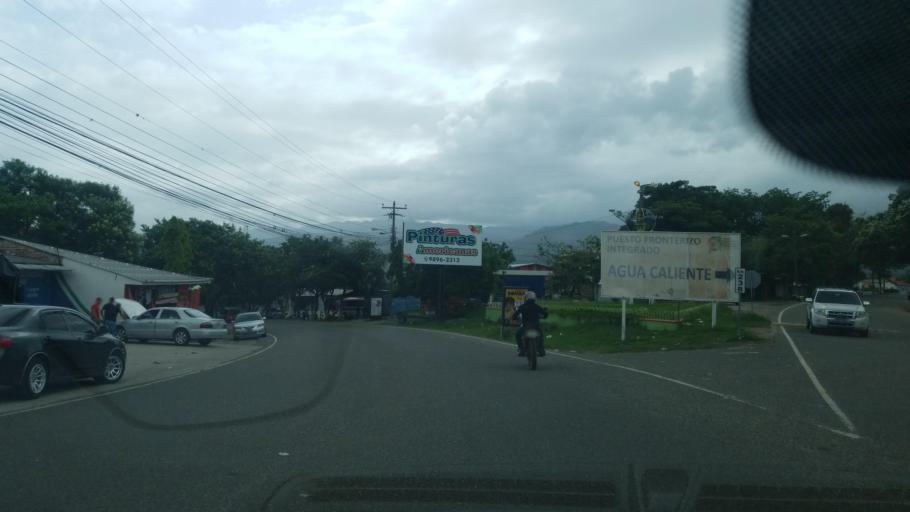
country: HN
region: Ocotepeque
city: Nueva Ocotepeque
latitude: 14.4415
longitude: -89.1830
